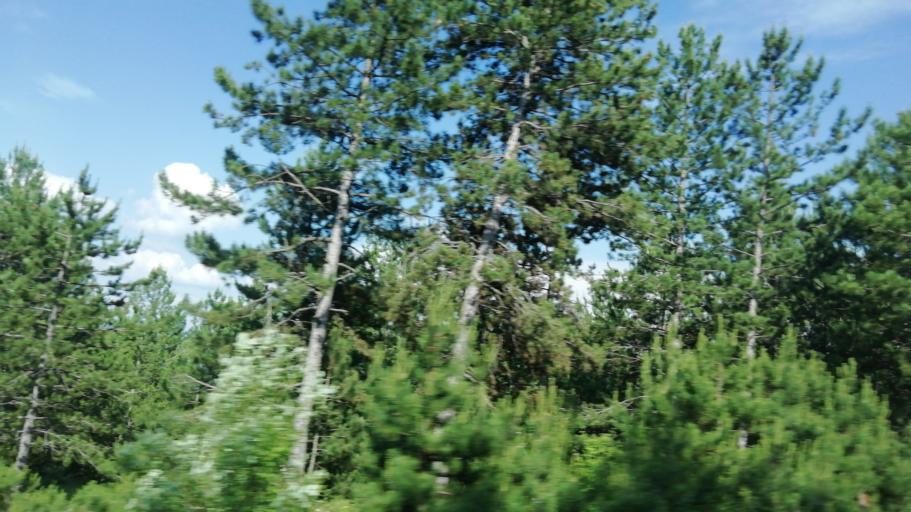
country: TR
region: Karabuk
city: Karabuk
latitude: 41.1227
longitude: 32.6050
